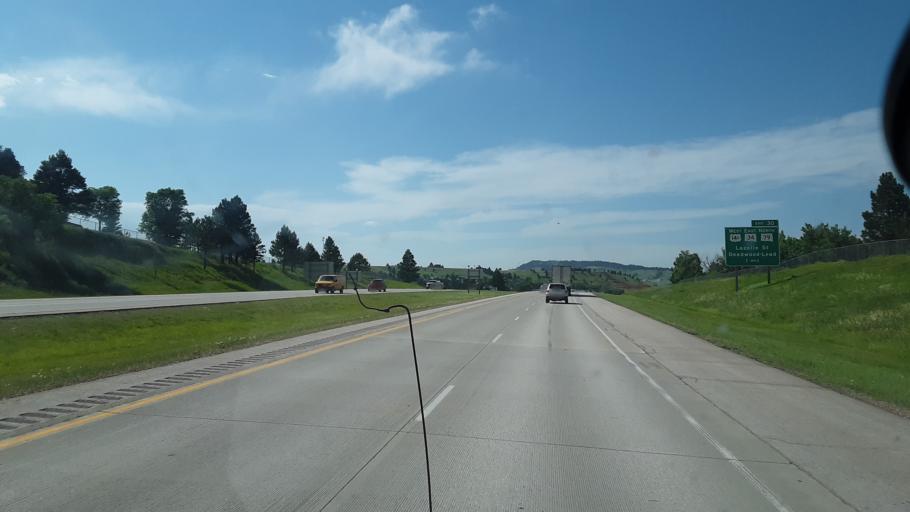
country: US
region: South Dakota
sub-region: Meade County
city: Sturgis
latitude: 44.4000
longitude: -103.5164
